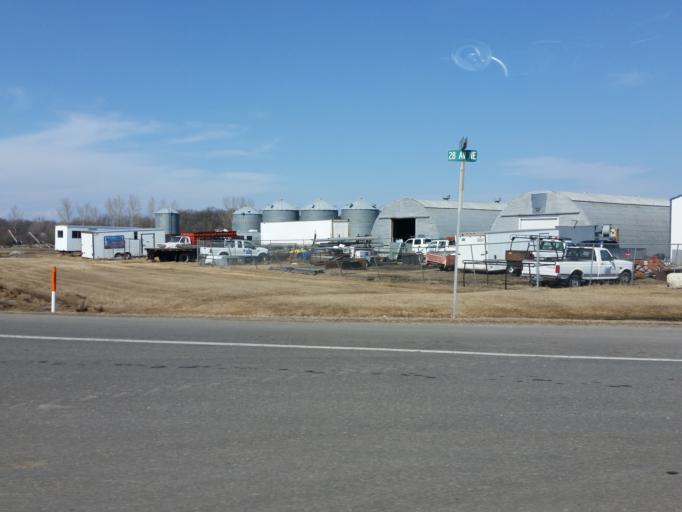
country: US
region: North Dakota
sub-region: Grand Forks County
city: Grand Forks
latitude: 48.0776
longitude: -97.1757
